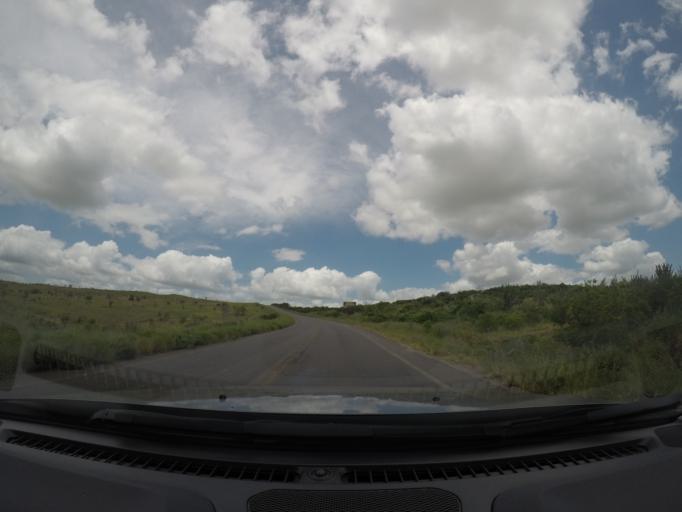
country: BR
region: Bahia
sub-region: Ipira
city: Ipira
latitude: -12.2547
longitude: -39.8182
